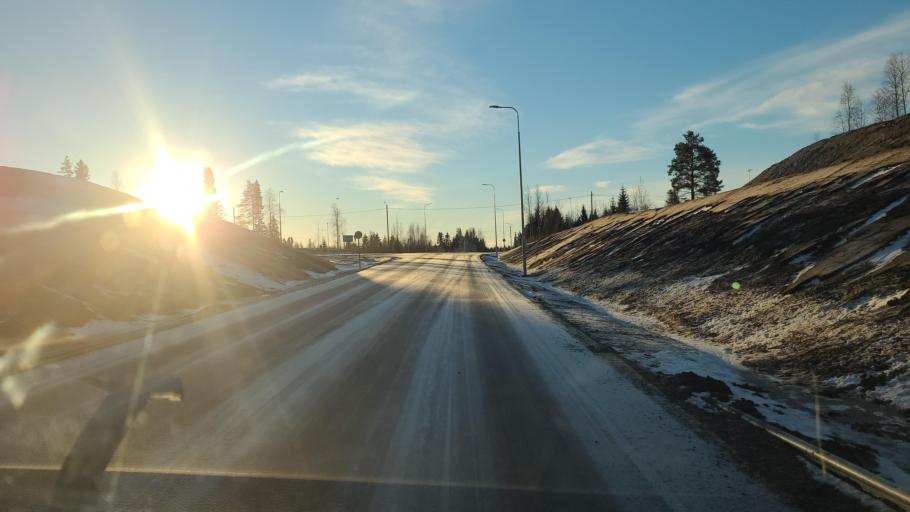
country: FI
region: Lapland
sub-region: Kemi-Tornio
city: Kemi
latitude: 65.6784
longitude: 24.7440
